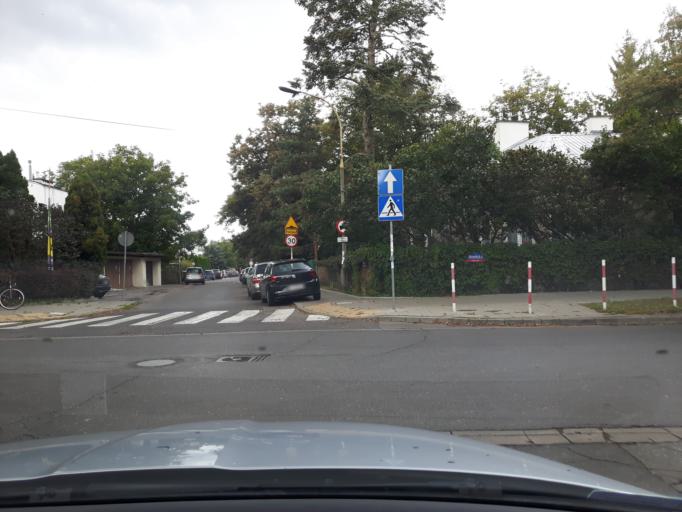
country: PL
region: Masovian Voivodeship
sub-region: Warszawa
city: Praga Poludnie
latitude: 52.2235
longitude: 21.0661
